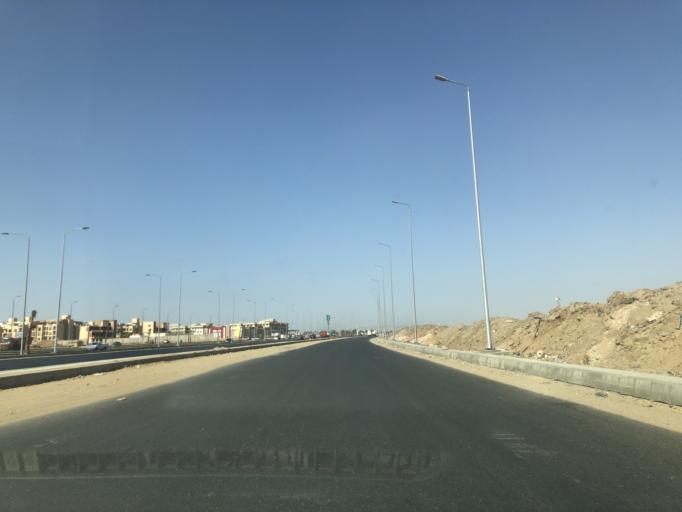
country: EG
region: Al Jizah
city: Madinat Sittah Uktubar
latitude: 29.9494
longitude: 30.9524
